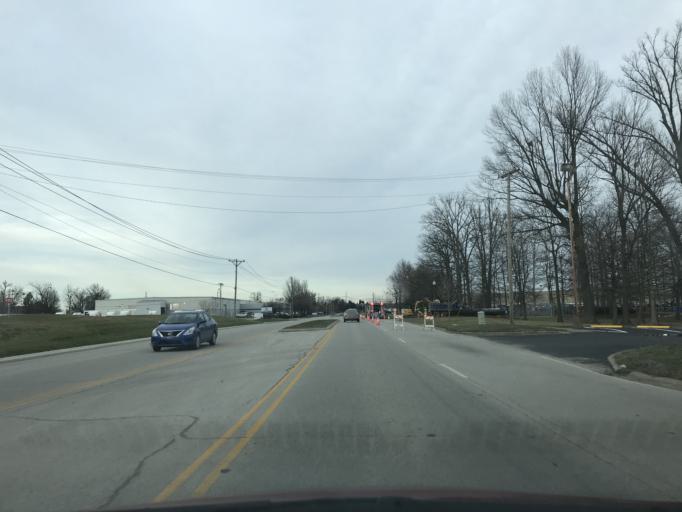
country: US
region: Kentucky
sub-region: Jefferson County
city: West Buechel
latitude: 38.1867
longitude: -85.6785
